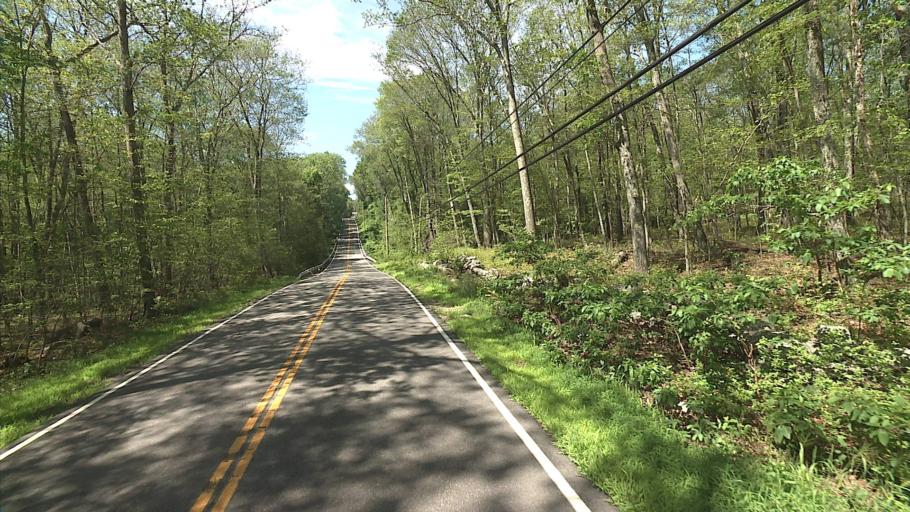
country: US
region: Connecticut
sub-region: Windham County
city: South Woodstock
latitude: 41.8983
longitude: -72.0238
